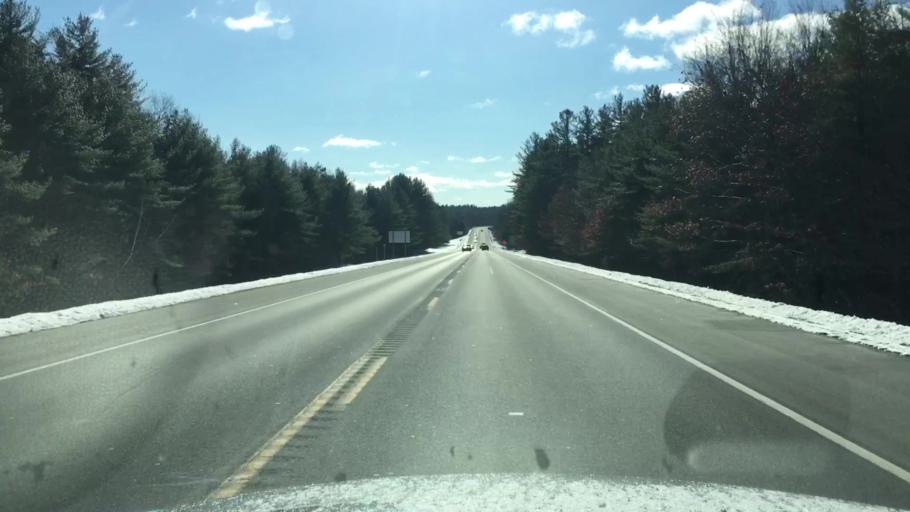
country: US
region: New Hampshire
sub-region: Hillsborough County
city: Milford
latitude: 42.8346
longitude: -71.6186
